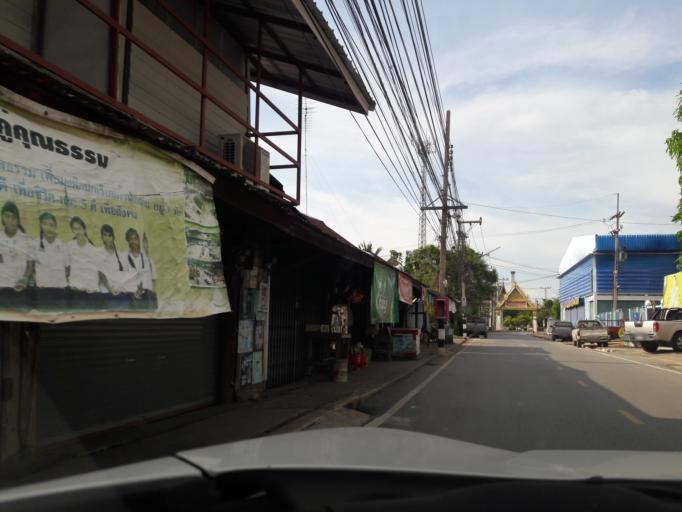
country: TH
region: Lop Buri
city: Ban Mi
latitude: 15.0445
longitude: 100.5387
